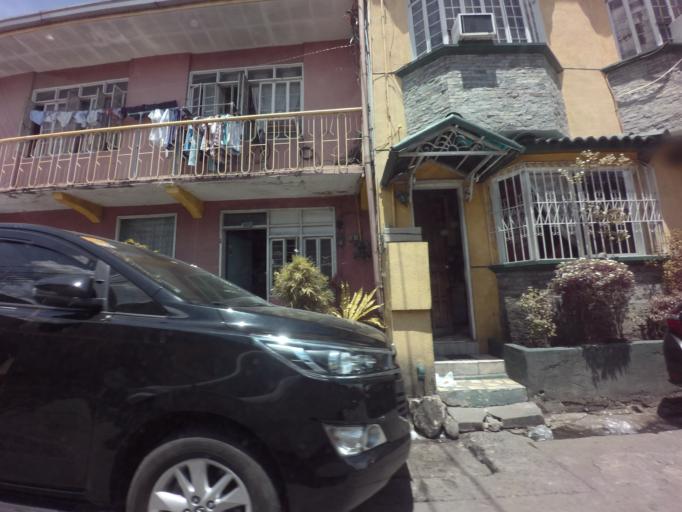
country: PH
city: Sambayanihan People's Village
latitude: 14.4981
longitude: 120.9914
